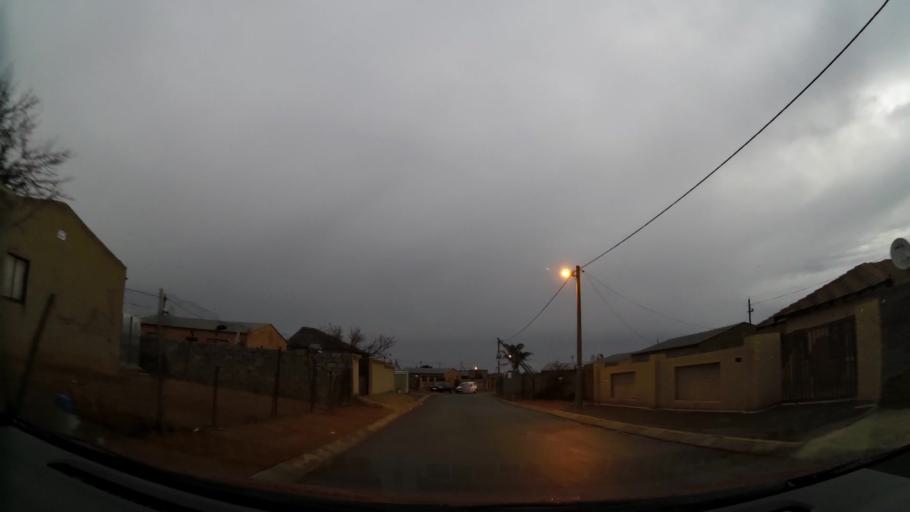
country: ZA
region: Gauteng
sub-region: West Rand District Municipality
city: Randfontein
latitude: -26.1772
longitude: 27.7861
